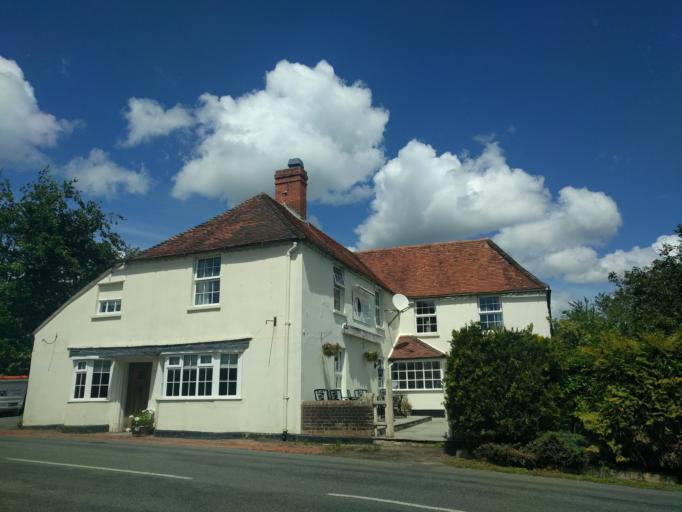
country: GB
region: England
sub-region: West Berkshire
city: Kintbury
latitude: 51.3861
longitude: -1.4062
